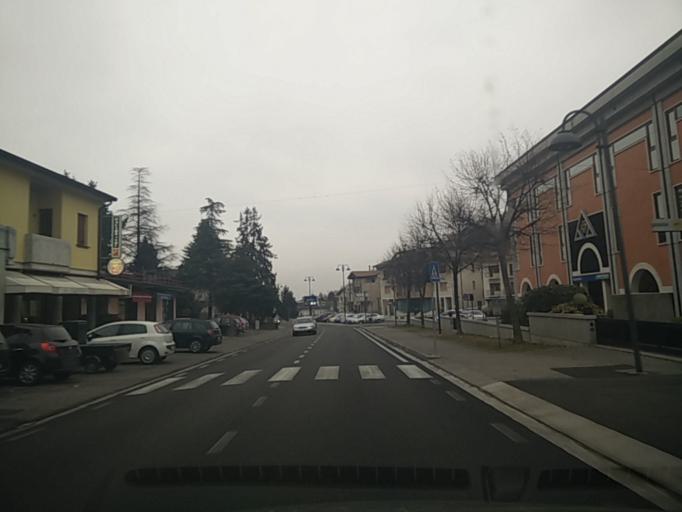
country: IT
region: Veneto
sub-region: Provincia di Treviso
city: Tarzo
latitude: 45.9749
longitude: 12.2311
